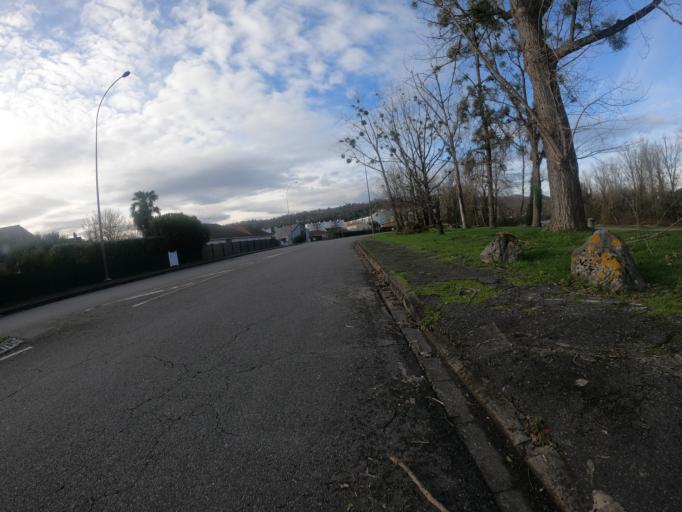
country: FR
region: Aquitaine
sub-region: Departement des Pyrenees-Atlantiques
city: Jurancon
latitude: 43.2921
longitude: -0.3911
